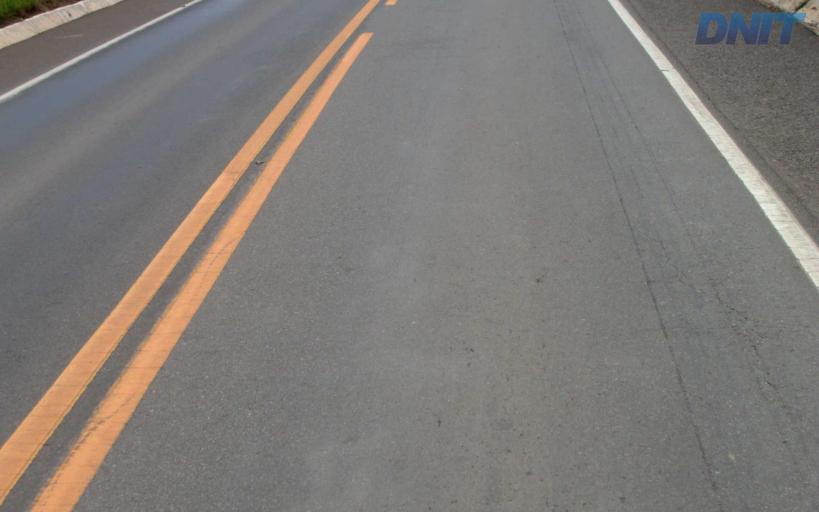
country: BR
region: Minas Gerais
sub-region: Governador Valadares
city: Governador Valadares
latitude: -19.0109
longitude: -42.1379
